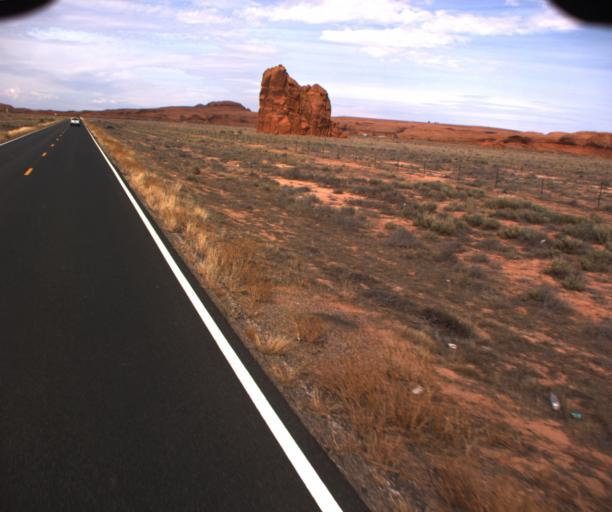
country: US
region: Arizona
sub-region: Apache County
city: Many Farms
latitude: 36.7444
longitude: -109.6393
